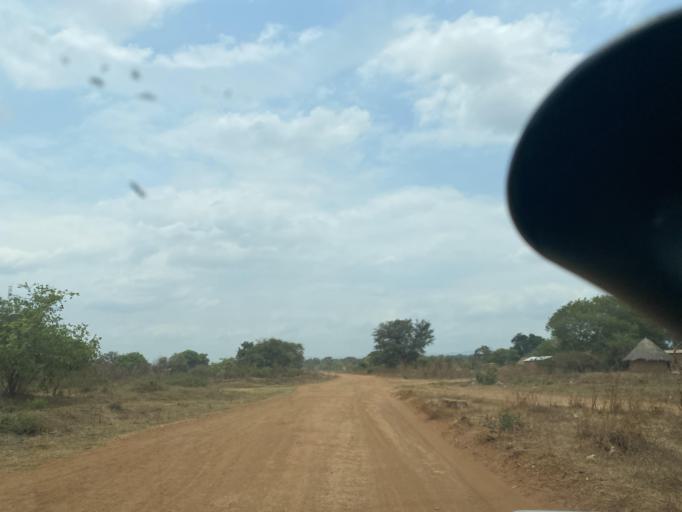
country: ZM
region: Lusaka
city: Chongwe
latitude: -15.5058
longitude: 28.8153
